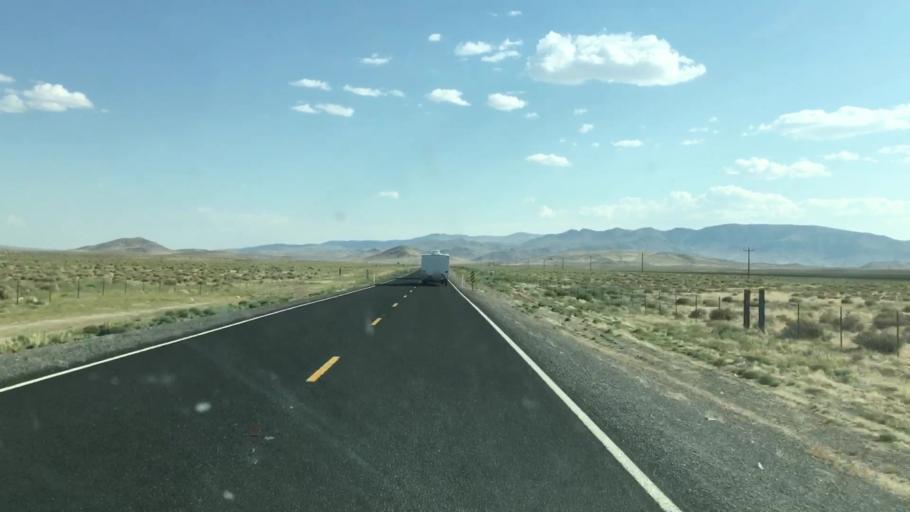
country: US
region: Nevada
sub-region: Lyon County
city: Fernley
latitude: 39.6698
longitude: -119.3320
